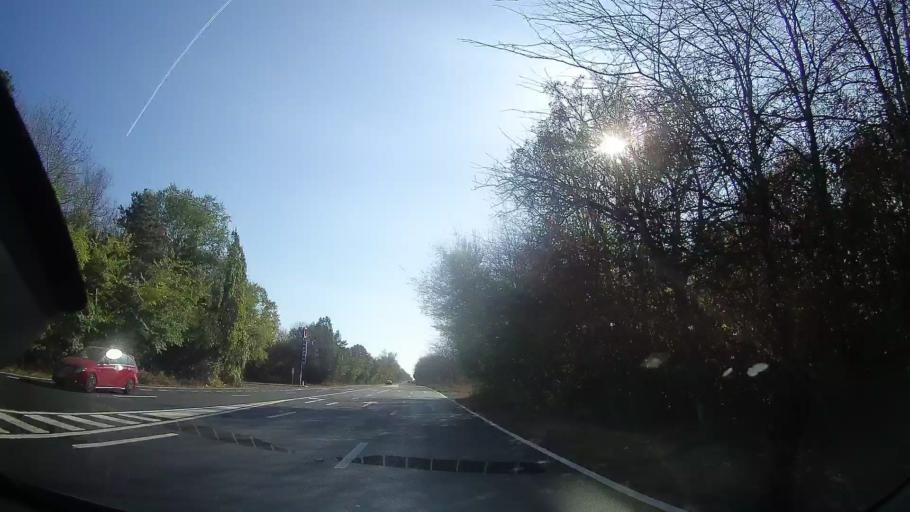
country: RO
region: Constanta
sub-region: Comuna Douazeci si Trei August
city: Dulcesti
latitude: 43.8757
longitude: 28.5739
